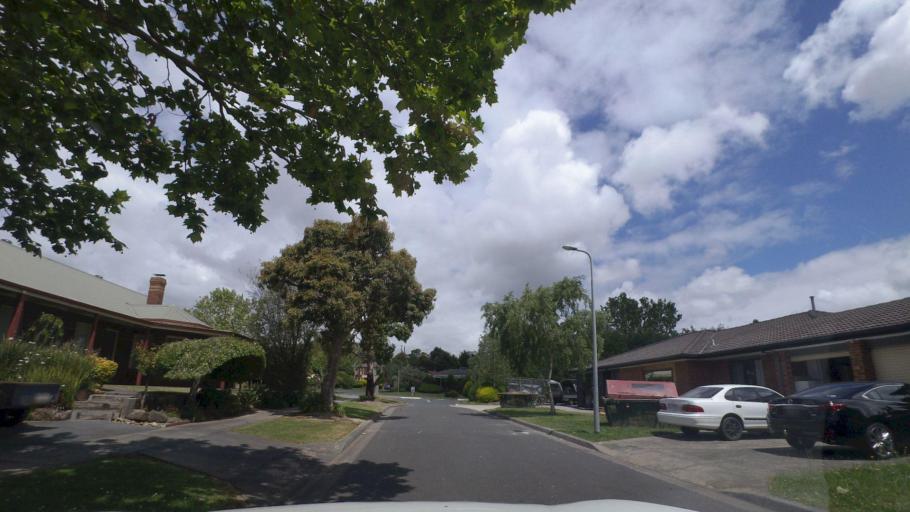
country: AU
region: Victoria
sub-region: Knox
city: Ferntree Gully
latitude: -37.9053
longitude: 145.2788
